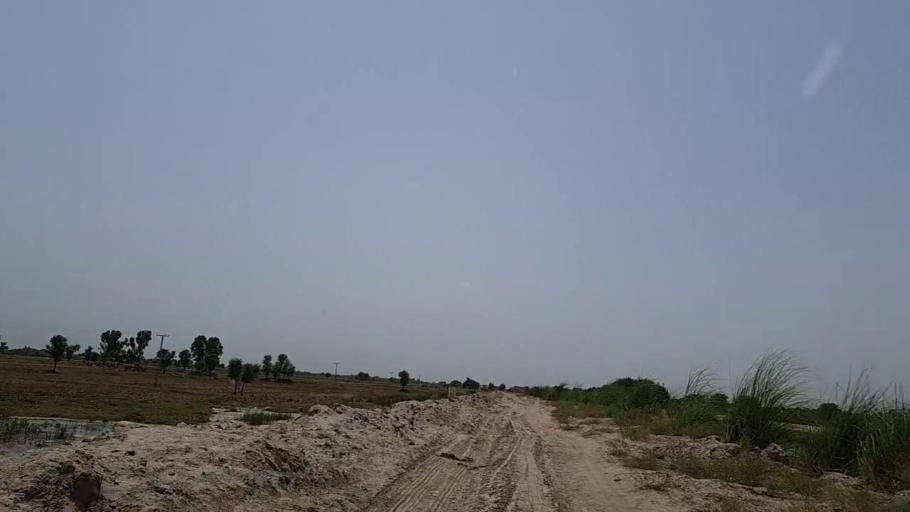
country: PK
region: Sindh
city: Tharu Shah
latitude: 26.9895
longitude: 68.0923
